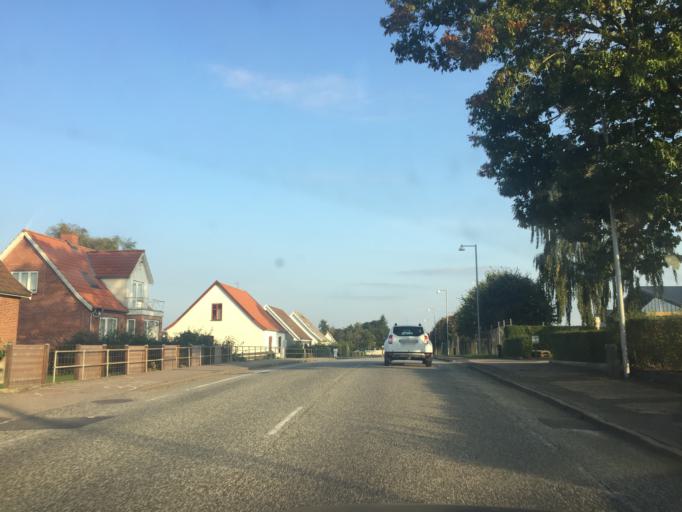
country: DK
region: Zealand
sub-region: Kalundborg Kommune
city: Hong
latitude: 55.5405
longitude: 11.3871
